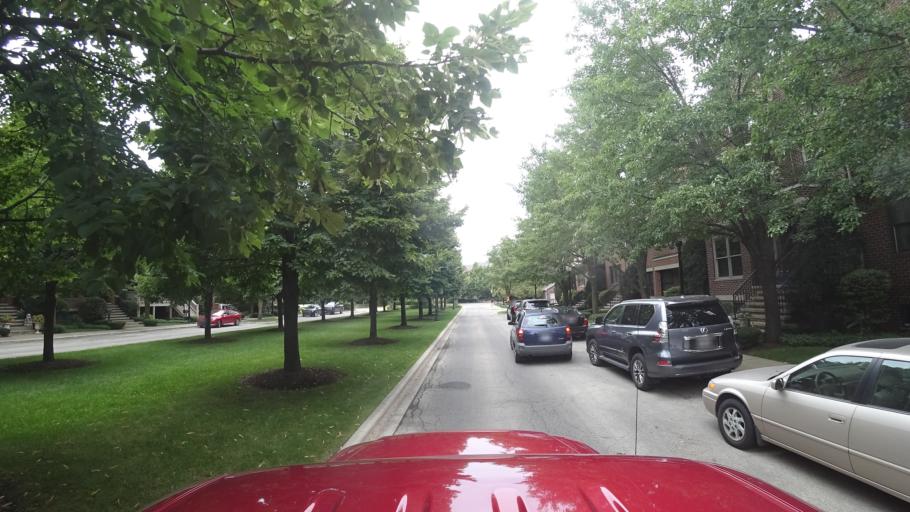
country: US
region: Illinois
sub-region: Cook County
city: Chicago
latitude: 41.8335
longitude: -87.6571
